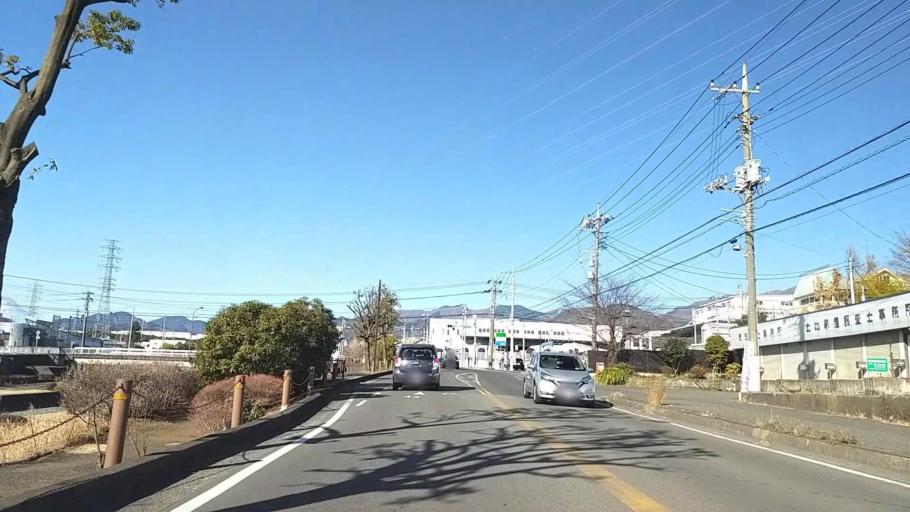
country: JP
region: Kanagawa
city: Hadano
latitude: 35.3830
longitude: 139.2002
